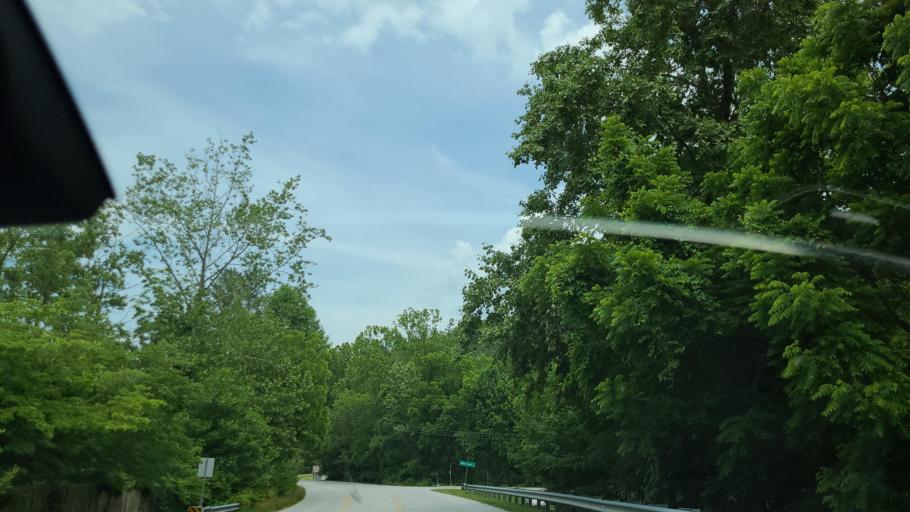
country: US
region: North Carolina
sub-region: Macon County
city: Franklin
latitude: 35.1356
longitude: -83.2810
